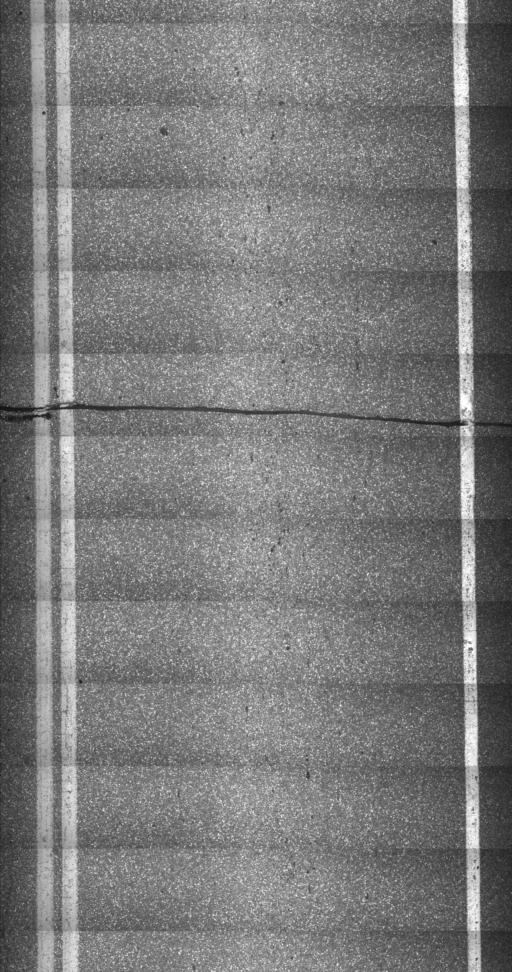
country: US
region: Vermont
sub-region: Windsor County
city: Wilder
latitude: 43.6726
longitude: -72.3092
